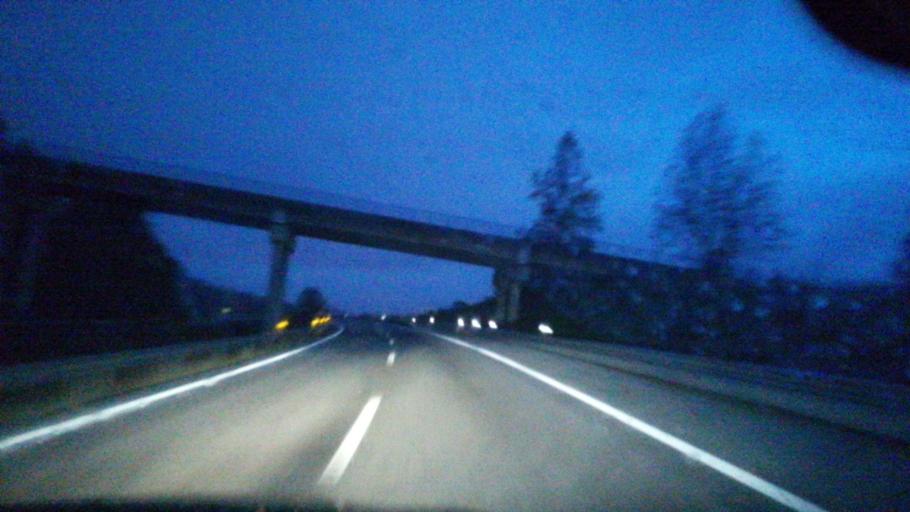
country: PT
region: Braga
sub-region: Guimaraes
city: Candoso
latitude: 41.4172
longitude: -8.3248
